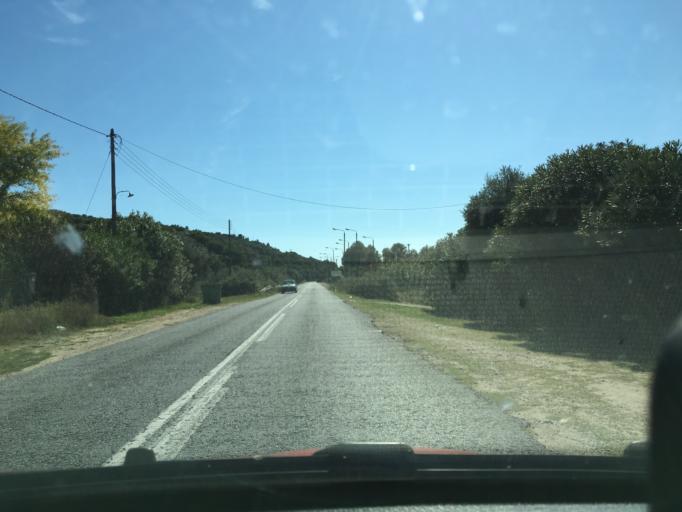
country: GR
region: Central Macedonia
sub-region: Nomos Chalkidikis
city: Ouranoupolis
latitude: 40.3414
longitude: 23.9698
